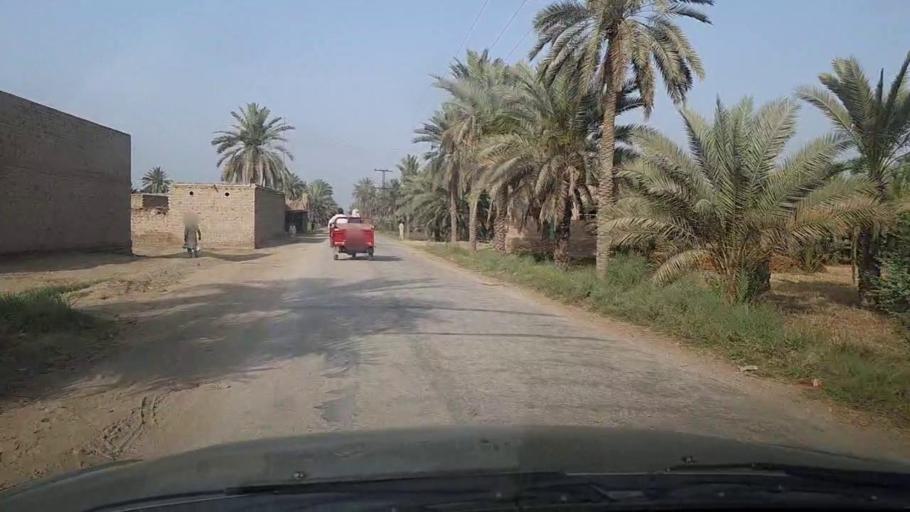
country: PK
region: Sindh
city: Pir jo Goth
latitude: 27.5663
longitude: 68.5781
